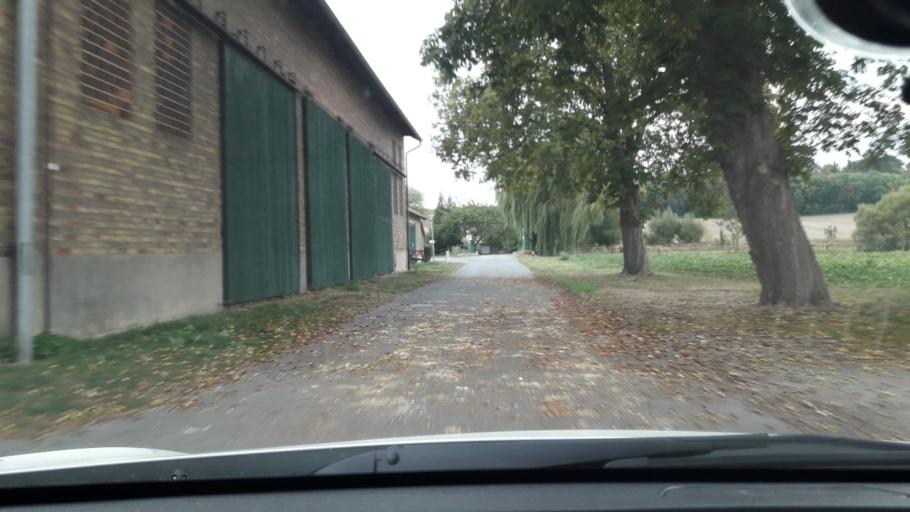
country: DE
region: Lower Saxony
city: Gielde
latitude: 52.0349
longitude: 10.4911
